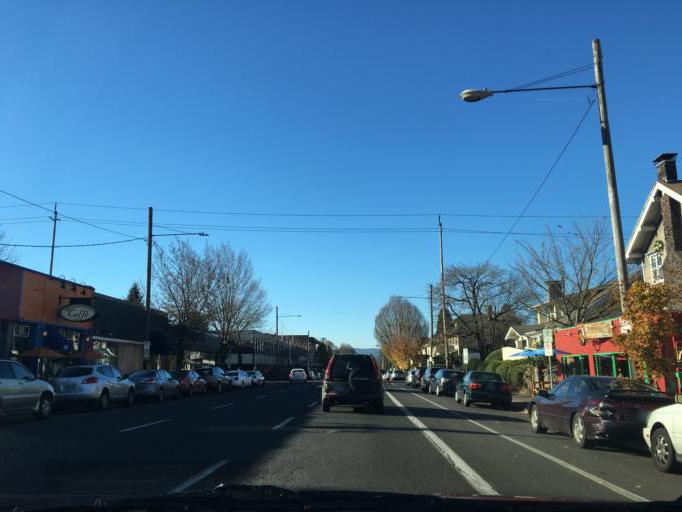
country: US
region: Oregon
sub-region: Multnomah County
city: Portland
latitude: 45.5351
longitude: -122.6420
